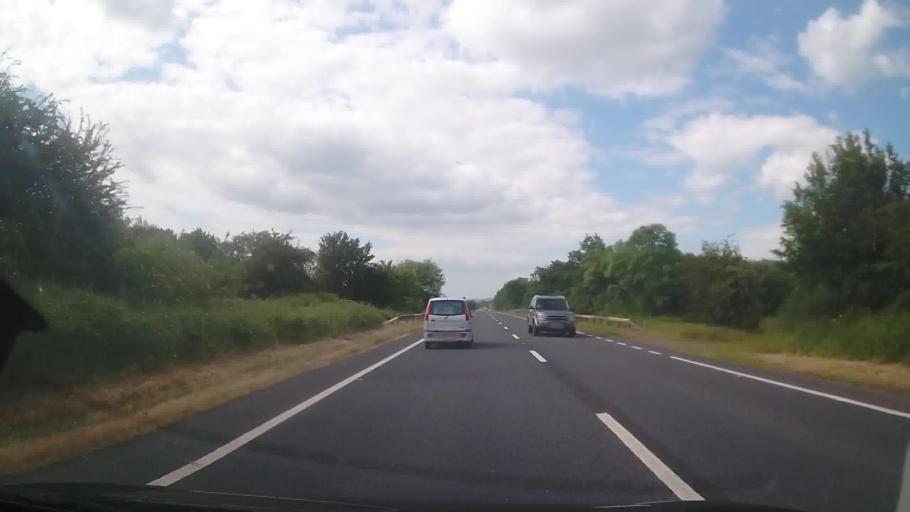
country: GB
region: England
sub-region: Herefordshire
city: Hope under Dinmore
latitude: 52.2069
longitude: -2.7219
